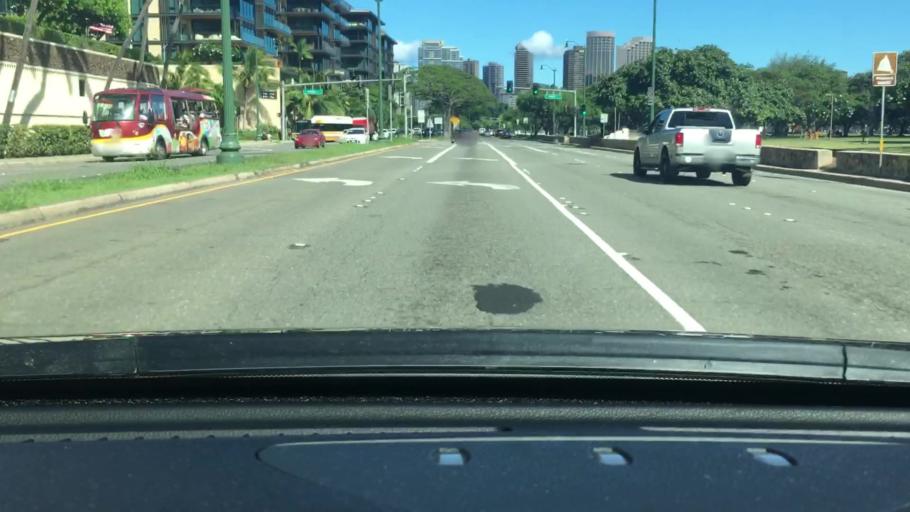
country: US
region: Hawaii
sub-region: Honolulu County
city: Honolulu
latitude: 21.2912
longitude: -157.8487
